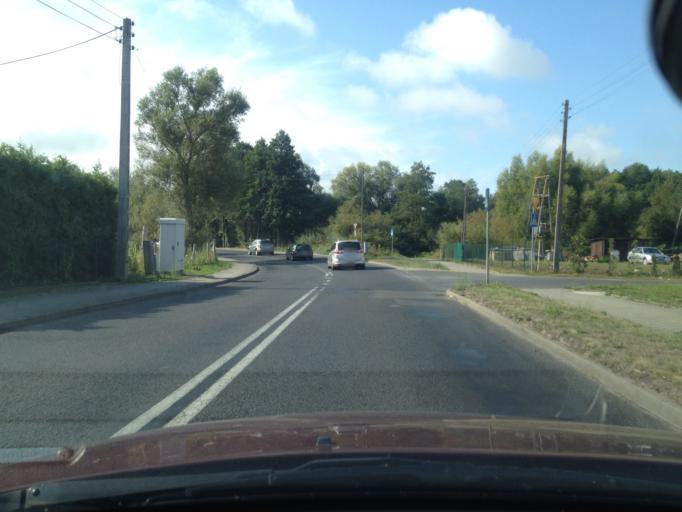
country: PL
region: West Pomeranian Voivodeship
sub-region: Powiat kamienski
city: Kamien Pomorski
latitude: 53.8878
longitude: 14.7898
